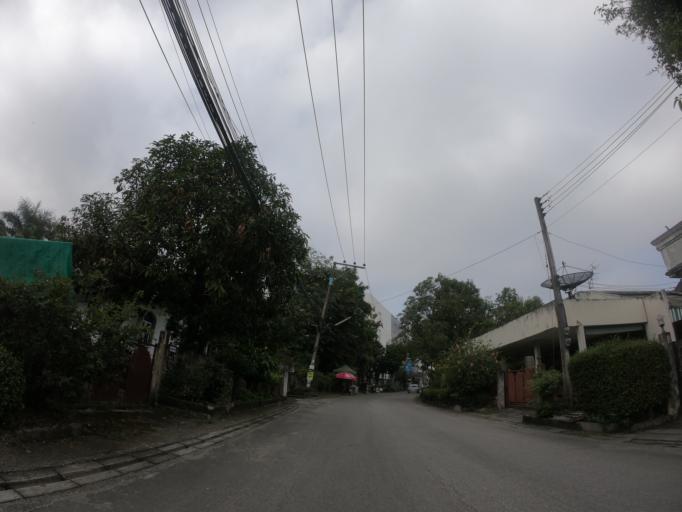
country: TH
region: Chiang Mai
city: Chiang Mai
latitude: 18.7619
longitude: 98.9738
